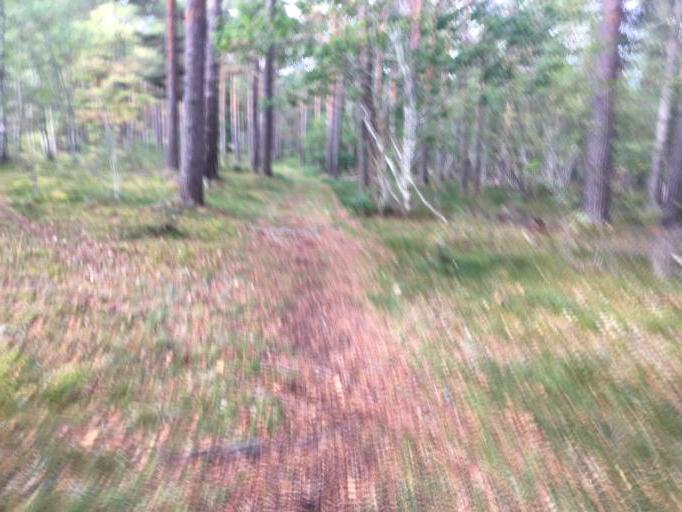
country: SE
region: Soedermanland
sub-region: Eskilstuna Kommun
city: Eskilstuna
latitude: 59.4365
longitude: 16.6342
